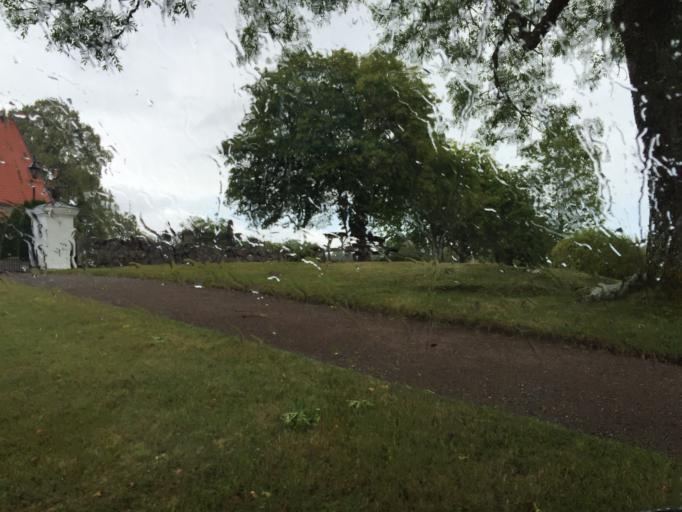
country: SE
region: Kalmar
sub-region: Vasterviks Kommun
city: Gamleby
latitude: 57.8028
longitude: 16.4633
